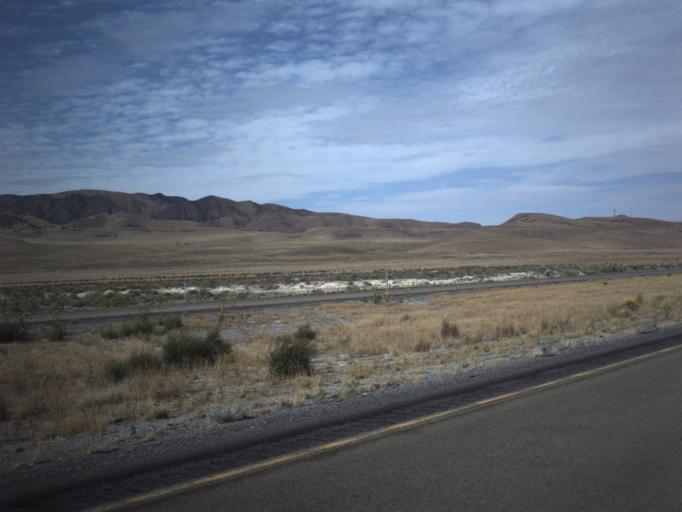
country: US
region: Utah
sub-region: Tooele County
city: Grantsville
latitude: 40.7862
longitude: -112.8238
